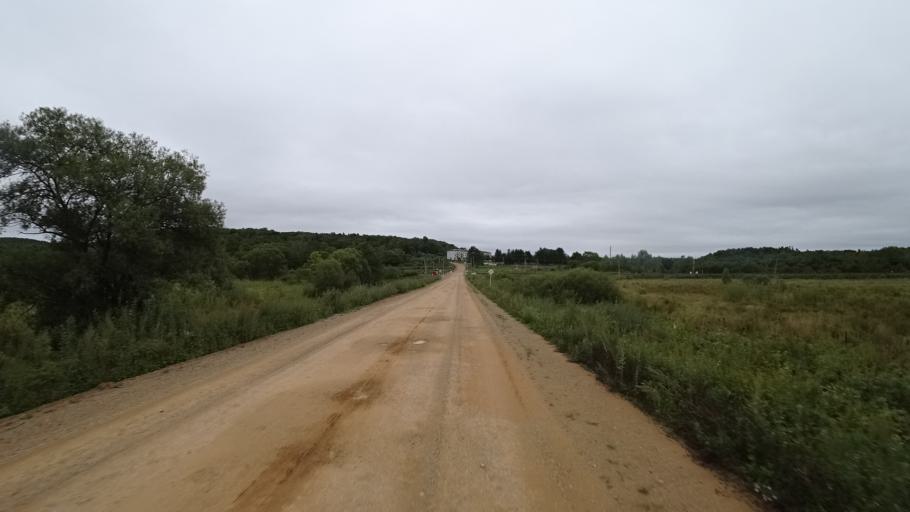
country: RU
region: Primorskiy
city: Rettikhovka
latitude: 44.1752
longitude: 132.8774
